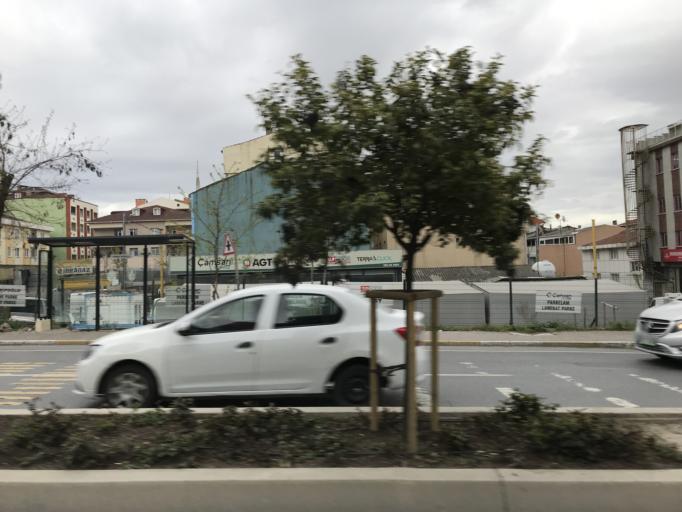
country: TR
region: Istanbul
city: Umraniye
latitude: 41.0097
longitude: 29.1638
